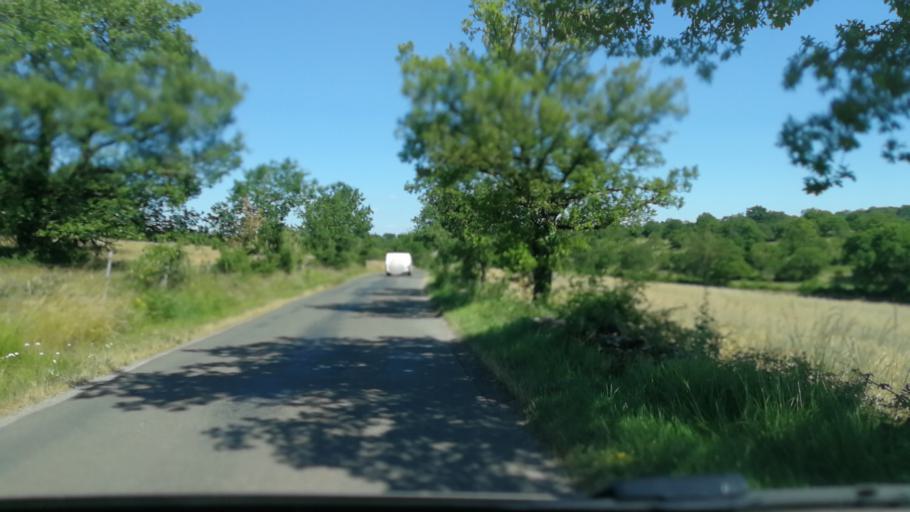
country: FR
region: Midi-Pyrenees
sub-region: Departement de l'Aveyron
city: Salles-la-Source
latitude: 44.4224
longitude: 2.5554
